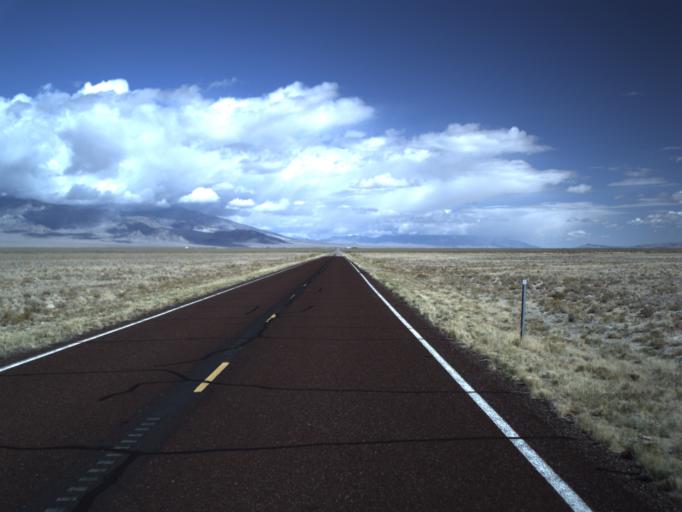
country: US
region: Nevada
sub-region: White Pine County
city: McGill
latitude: 38.9842
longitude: -114.0343
